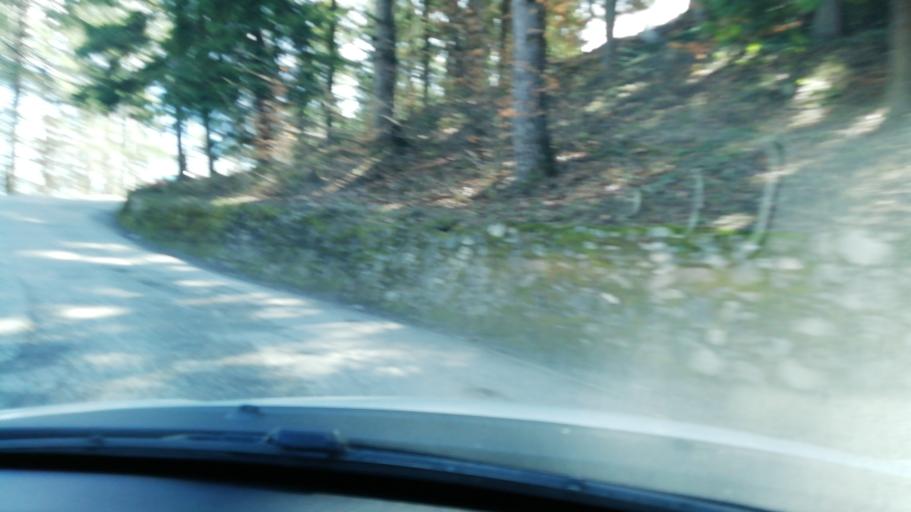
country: MK
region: Krusevo
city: Krushevo
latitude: 41.3639
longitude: 21.2506
